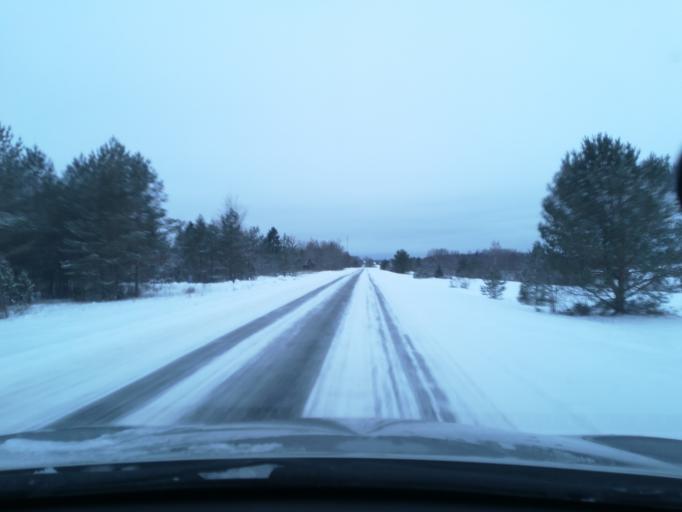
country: EE
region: Harju
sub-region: Keila linn
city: Keila
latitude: 59.3664
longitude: 24.3284
